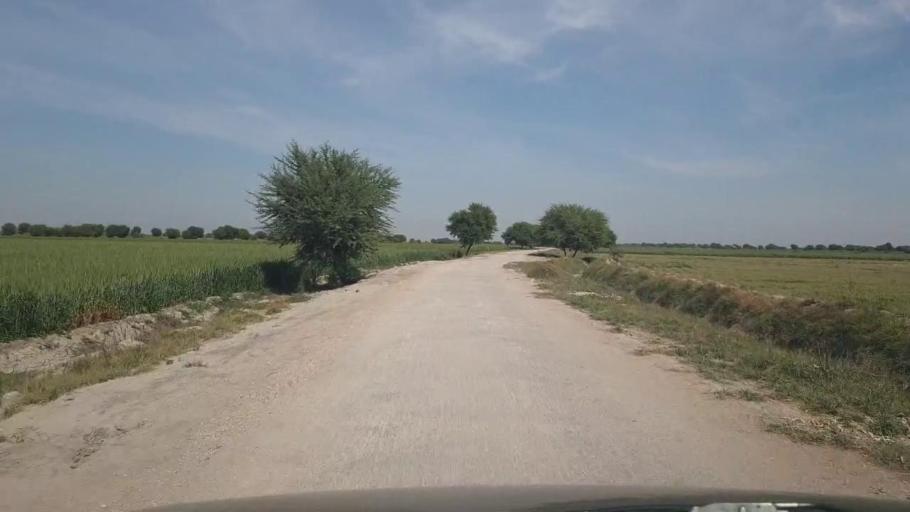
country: PK
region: Sindh
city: Kunri
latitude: 25.2168
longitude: 69.6431
